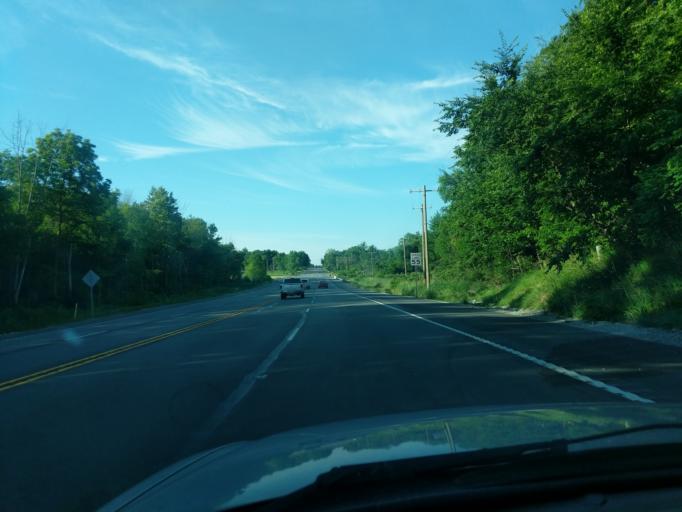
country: US
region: Indiana
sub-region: Madison County
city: Pendleton
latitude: 40.0253
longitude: -85.7300
